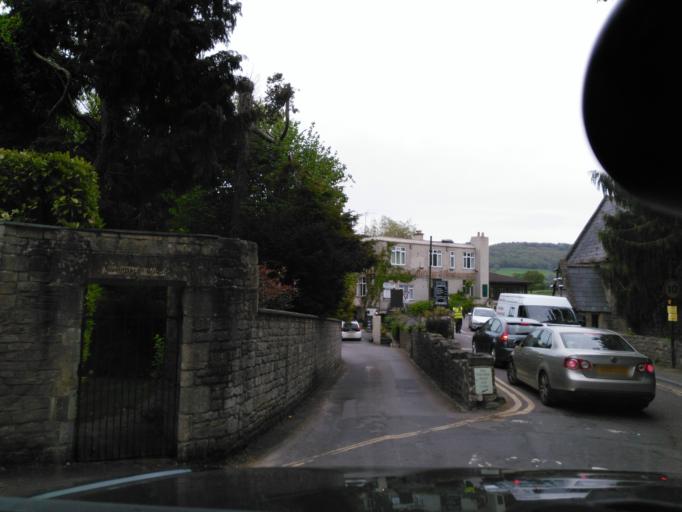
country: GB
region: England
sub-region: Bath and North East Somerset
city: Bath
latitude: 51.4019
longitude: -2.3266
